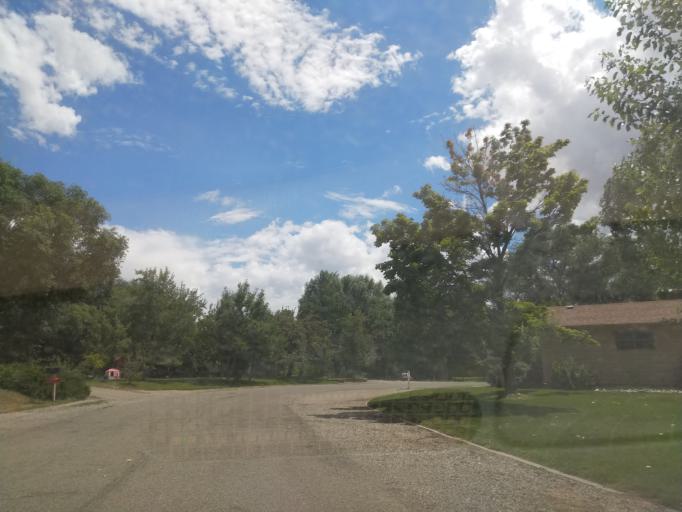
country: US
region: Colorado
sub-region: Mesa County
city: Redlands
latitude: 39.0689
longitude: -108.6483
